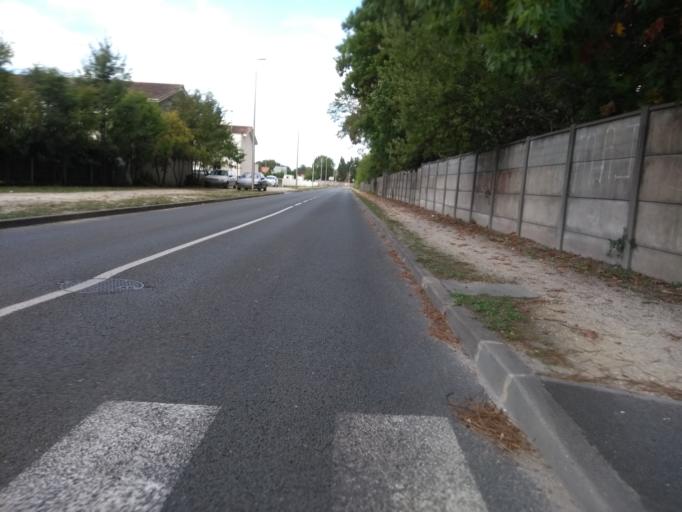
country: FR
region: Aquitaine
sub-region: Departement de la Gironde
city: Cestas
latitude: 44.7841
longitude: -0.6798
